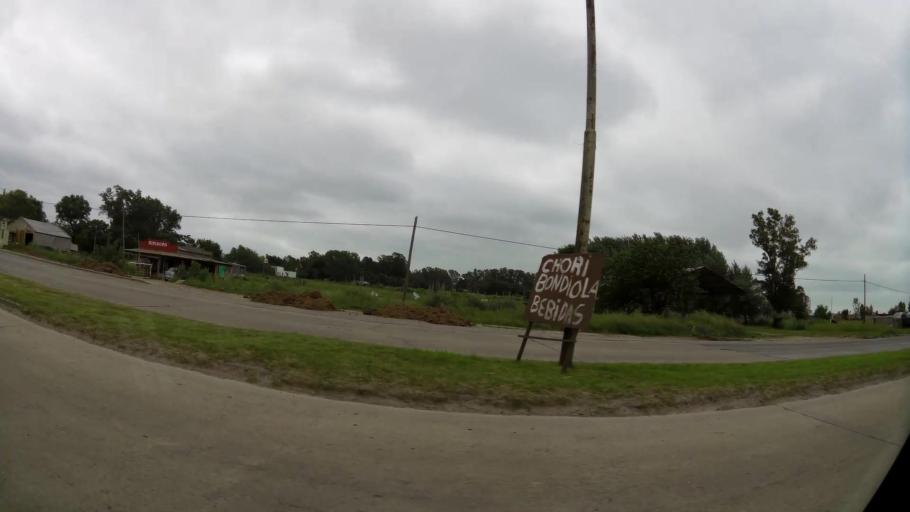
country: AR
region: Buenos Aires
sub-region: Partido de Brandsen
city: Brandsen
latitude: -35.0494
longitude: -58.1074
